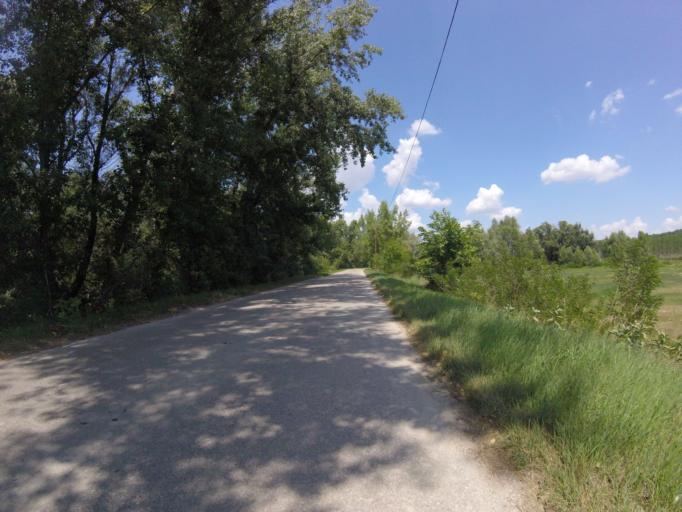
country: HU
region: Fejer
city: Adony
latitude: 47.1180
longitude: 18.8908
